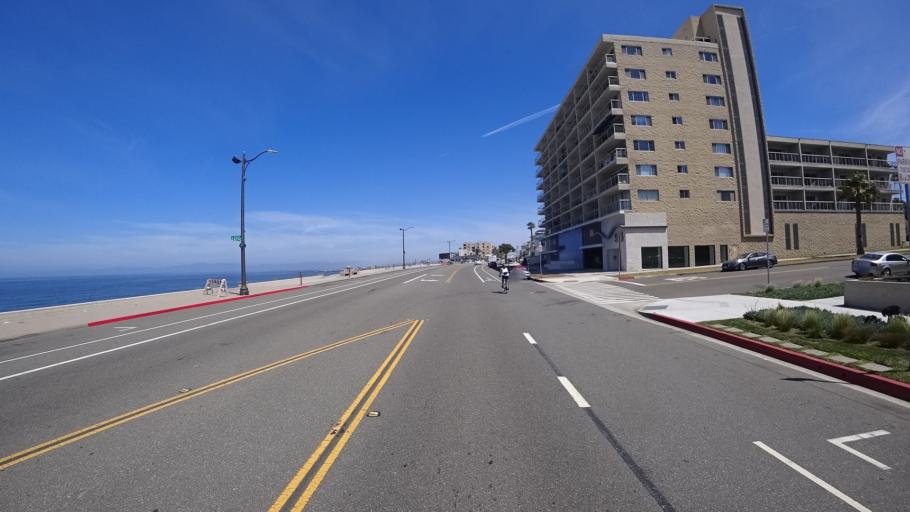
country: US
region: California
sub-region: Los Angeles County
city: Redondo Beach
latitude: 33.8263
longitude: -118.3900
